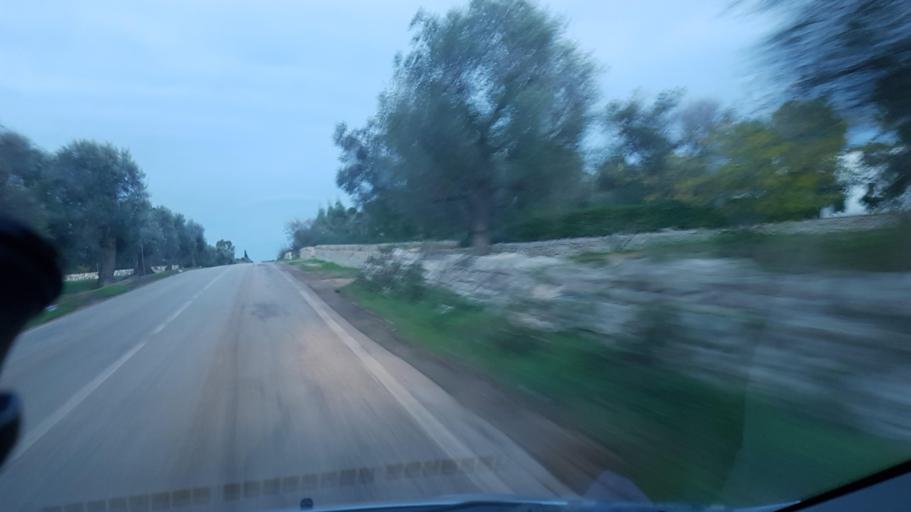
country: IT
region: Apulia
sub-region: Provincia di Brindisi
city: San Michele Salentino
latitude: 40.6444
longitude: 17.6031
